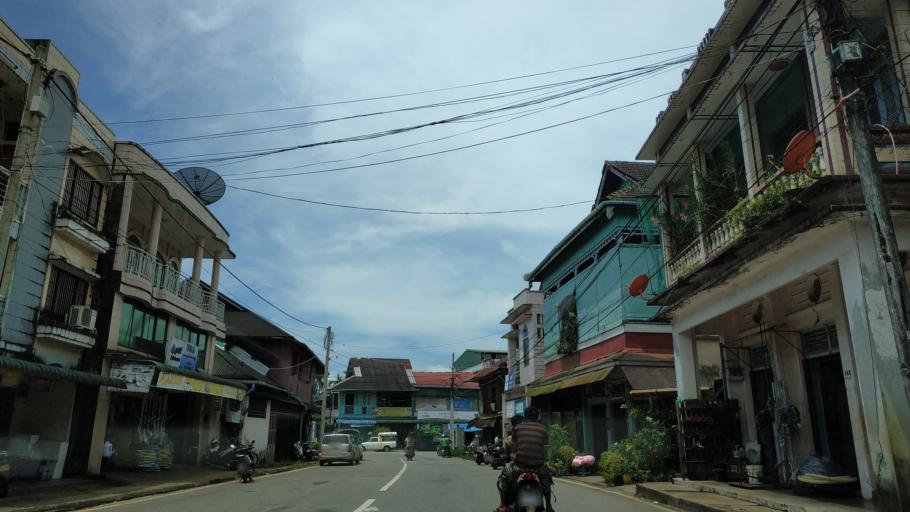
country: MM
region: Tanintharyi
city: Dawei
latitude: 14.0721
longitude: 98.1899
